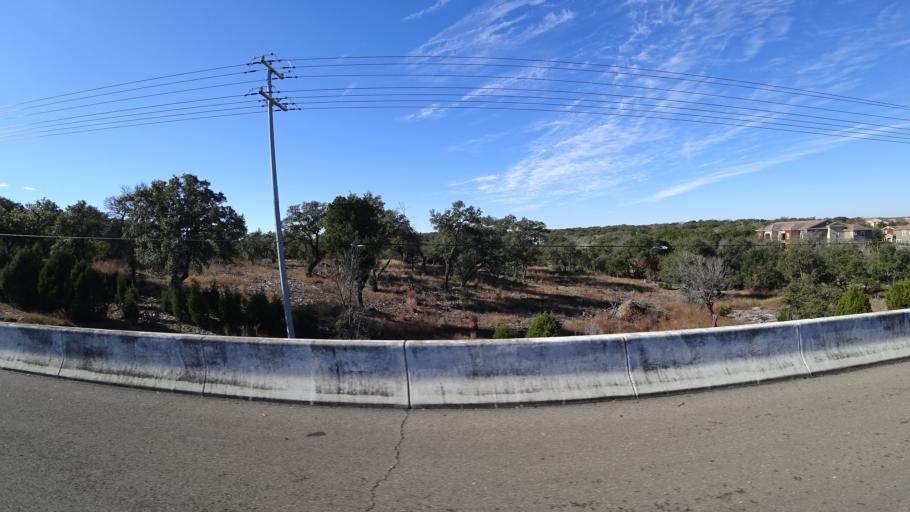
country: US
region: Texas
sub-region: Williamson County
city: Brushy Creek
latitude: 30.5272
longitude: -97.7771
